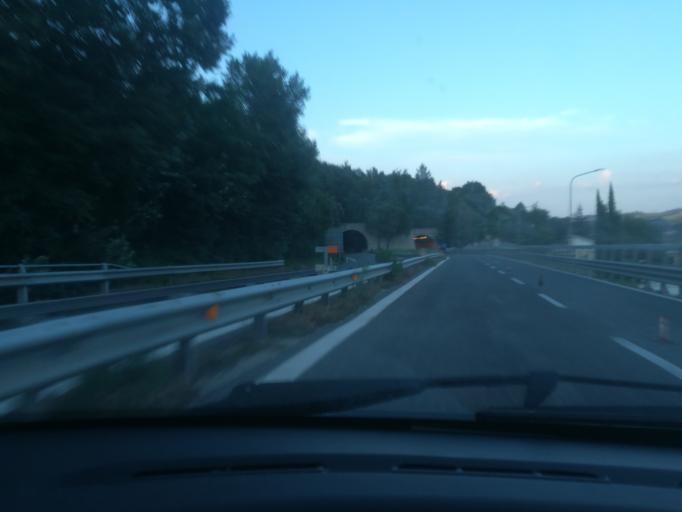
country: IT
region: The Marches
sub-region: Provincia di Macerata
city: Caldarola
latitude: 43.1469
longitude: 13.2021
